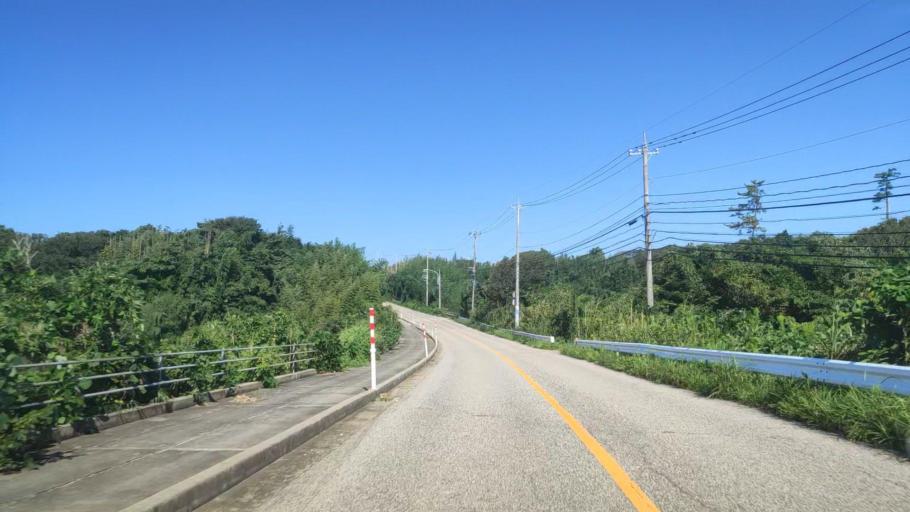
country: JP
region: Ishikawa
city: Hakui
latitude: 37.0508
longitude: 136.7352
